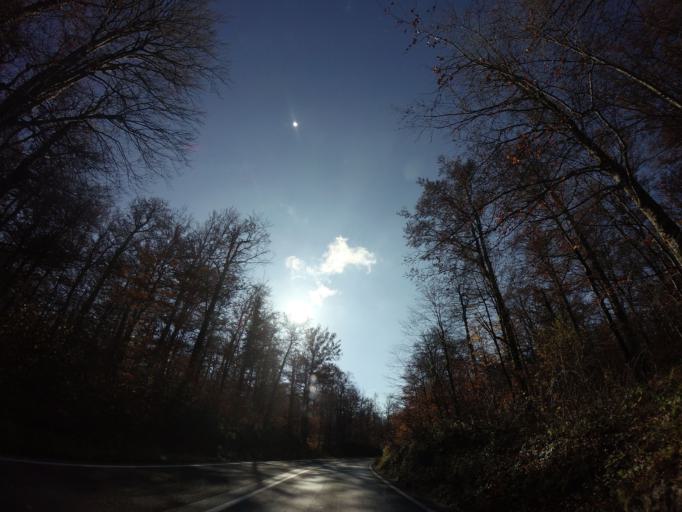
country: HR
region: Licko-Senjska
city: Jezerce
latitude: 44.8947
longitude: 15.6137
